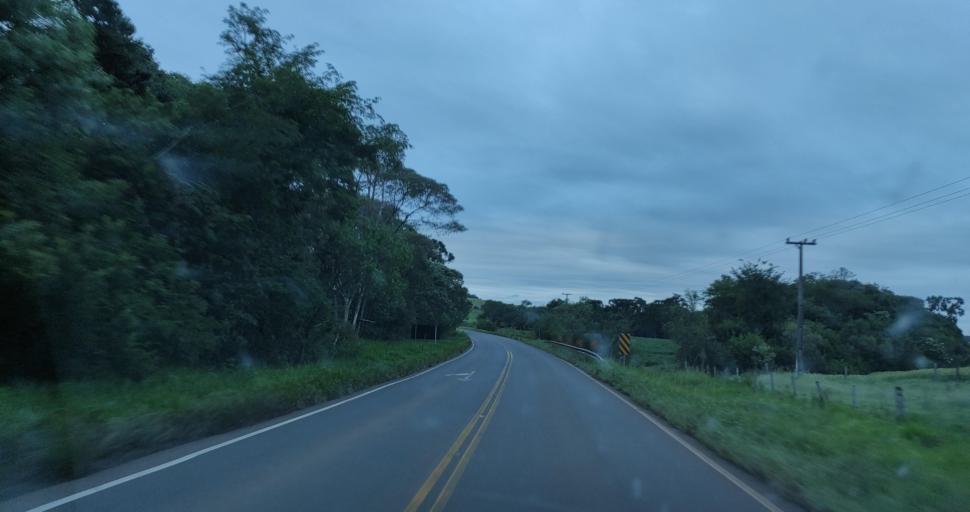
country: BR
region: Santa Catarina
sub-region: Xanxere
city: Xanxere
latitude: -26.7213
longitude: -52.4108
